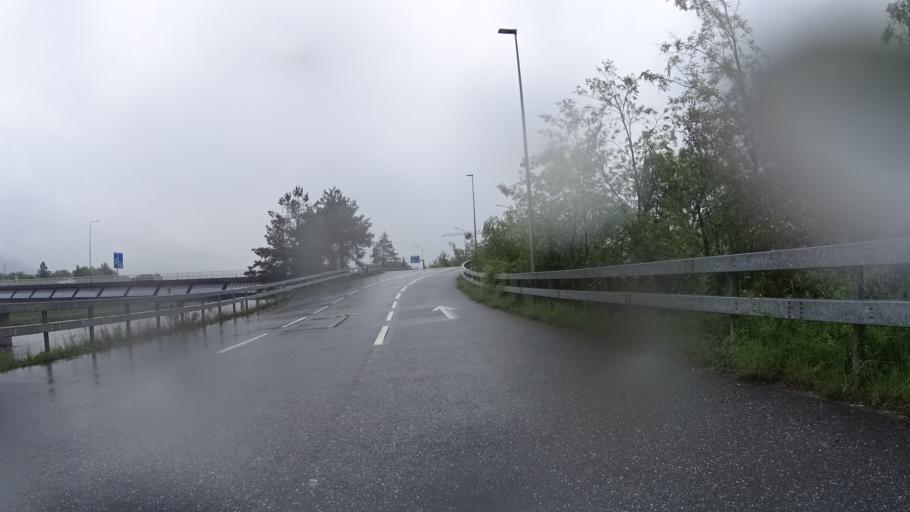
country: LI
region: Vaduz
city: Vaduz
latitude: 47.1298
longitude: 9.5137
